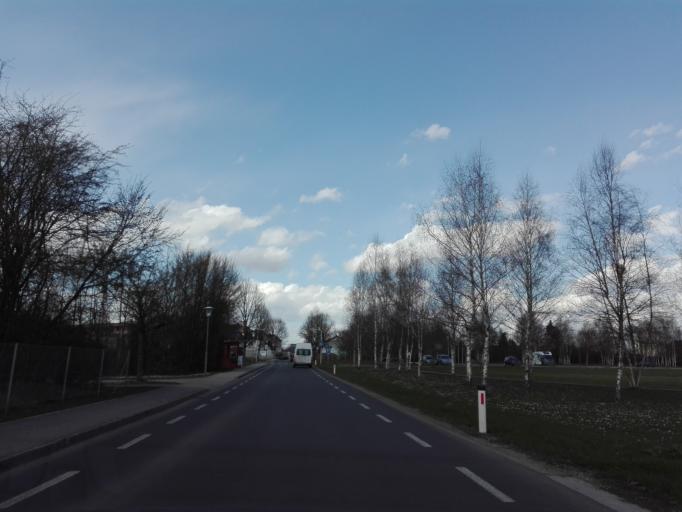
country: AT
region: Upper Austria
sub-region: Politischer Bezirk Urfahr-Umgebung
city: Goldworth
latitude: 48.2795
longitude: 14.1117
